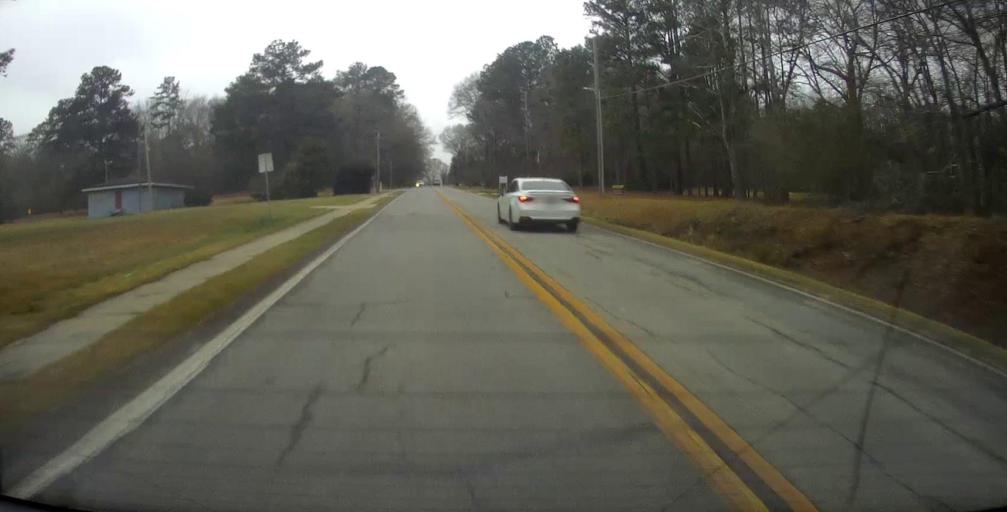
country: US
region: Georgia
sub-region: Lamar County
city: Barnesville
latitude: 33.0543
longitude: -84.1403
